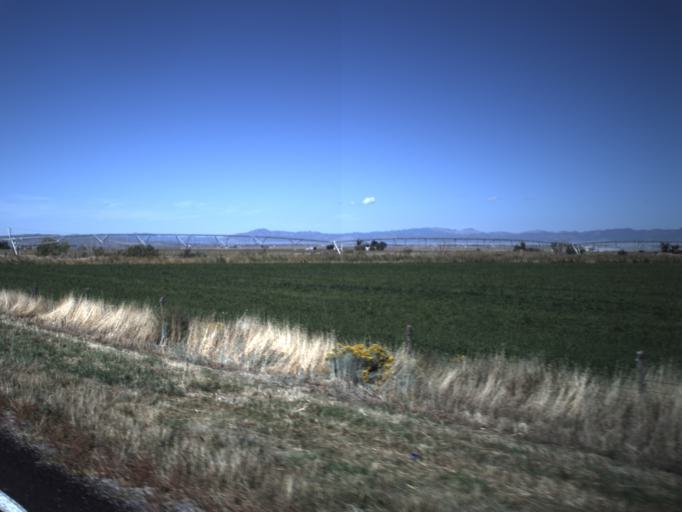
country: US
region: Utah
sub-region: Washington County
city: Enterprise
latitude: 37.6731
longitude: -113.5385
